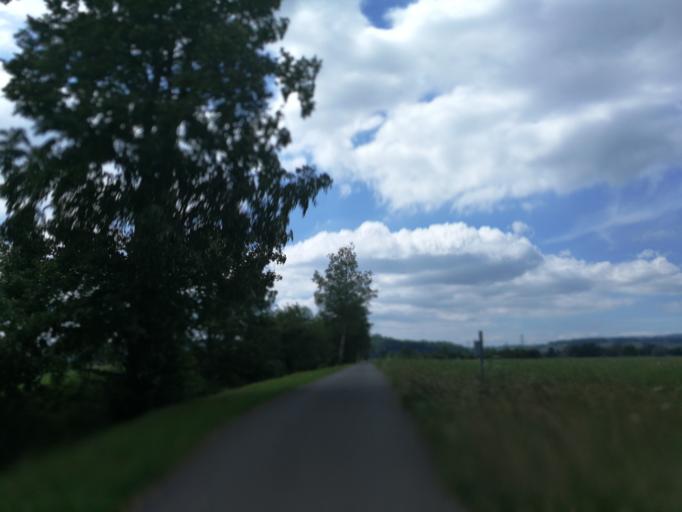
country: CH
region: Saint Gallen
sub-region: Wahlkreis See-Gaster
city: Uznach
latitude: 47.2094
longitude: 8.9866
